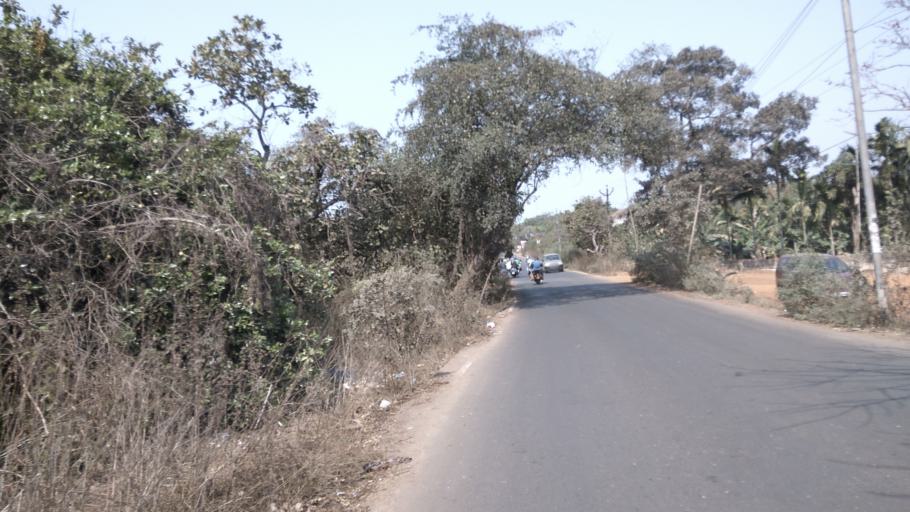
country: IN
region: Goa
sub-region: North Goa
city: Vagator
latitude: 15.5967
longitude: 73.7498
